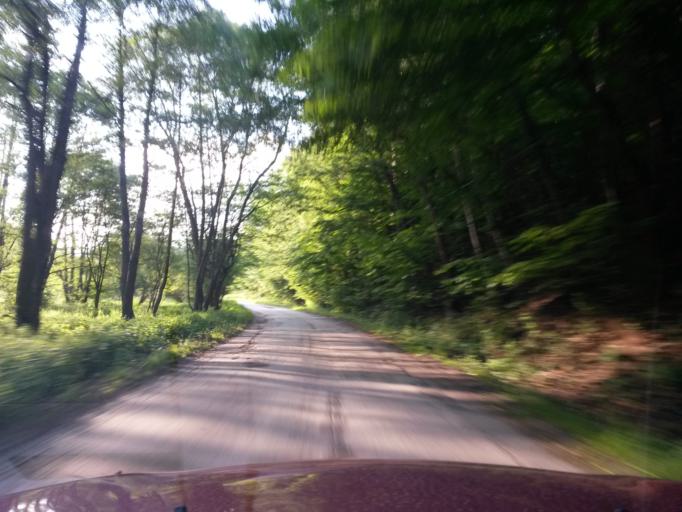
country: SK
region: Kosicky
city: Moldava nad Bodvou
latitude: 48.7345
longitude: 21.0297
